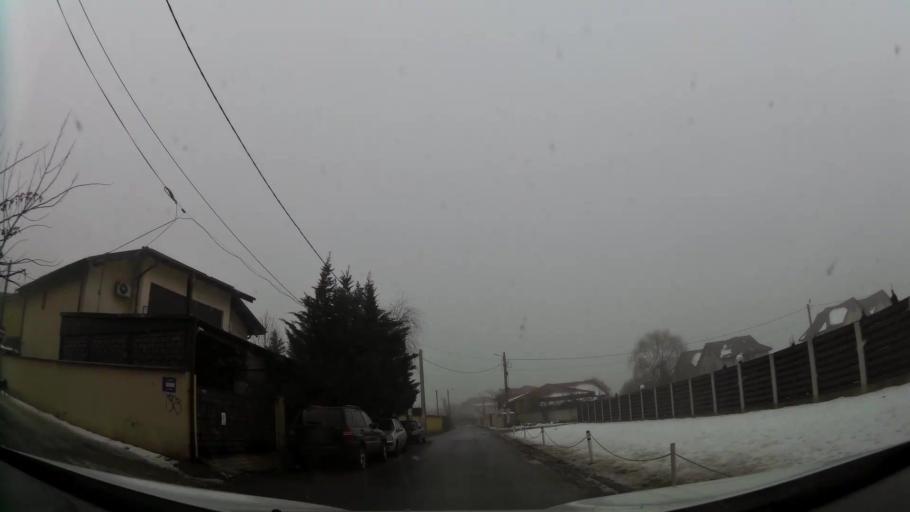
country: RO
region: Ilfov
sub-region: Comuna Chiajna
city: Chiajna
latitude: 44.4512
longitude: 25.9885
